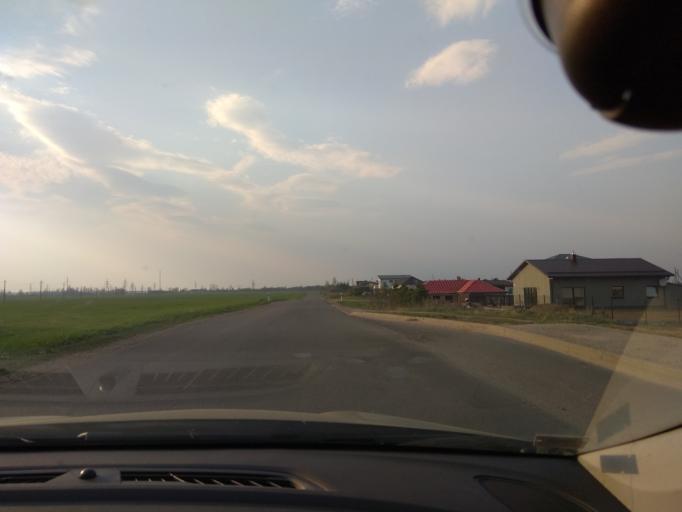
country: LT
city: Baltoji Voke
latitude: 54.6039
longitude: 25.1341
